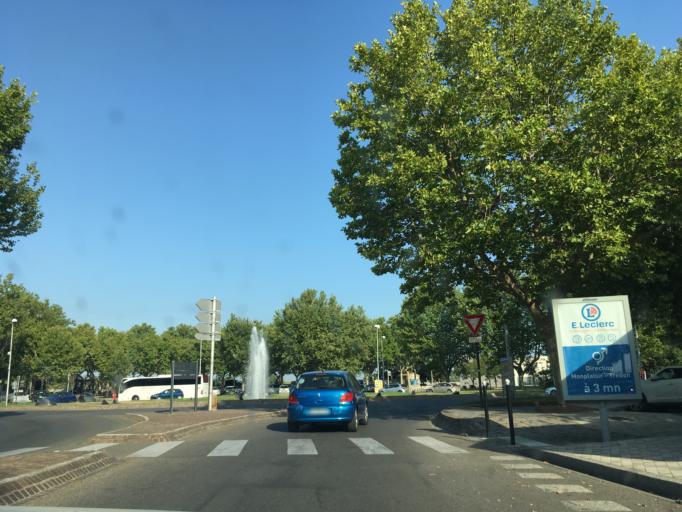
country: FR
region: Provence-Alpes-Cote d'Azur
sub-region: Departement des Bouches-du-Rhone
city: Arles
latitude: 43.6813
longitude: 4.6323
